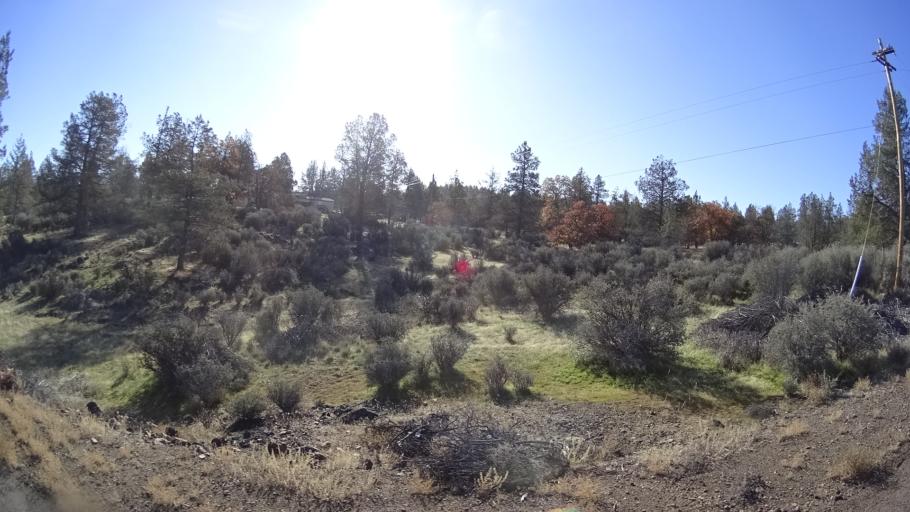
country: US
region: California
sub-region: Siskiyou County
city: Montague
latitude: 41.9159
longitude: -122.4263
